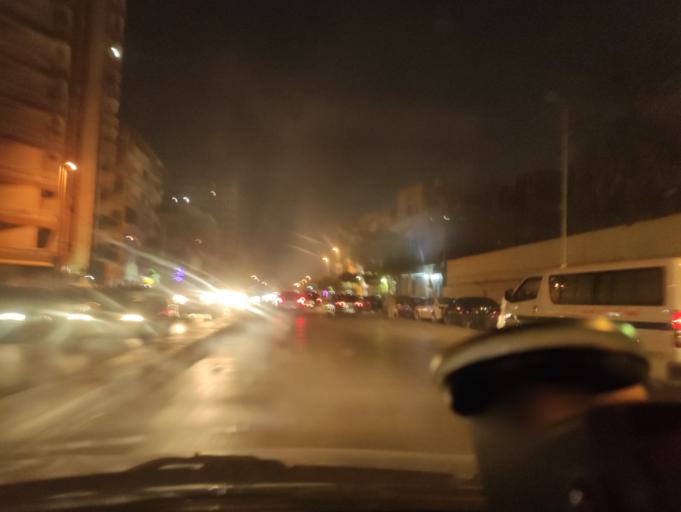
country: EG
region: Muhafazat al Qahirah
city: Cairo
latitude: 30.0917
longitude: 31.2796
